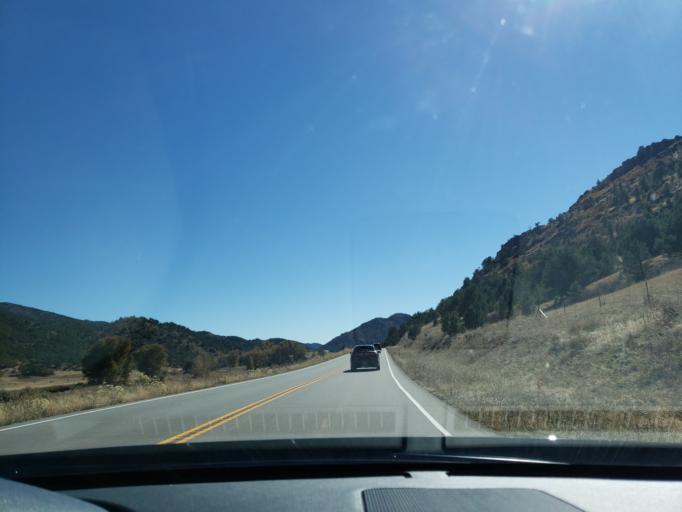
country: US
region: Colorado
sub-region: Fremont County
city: Canon City
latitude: 38.6018
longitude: -105.4307
